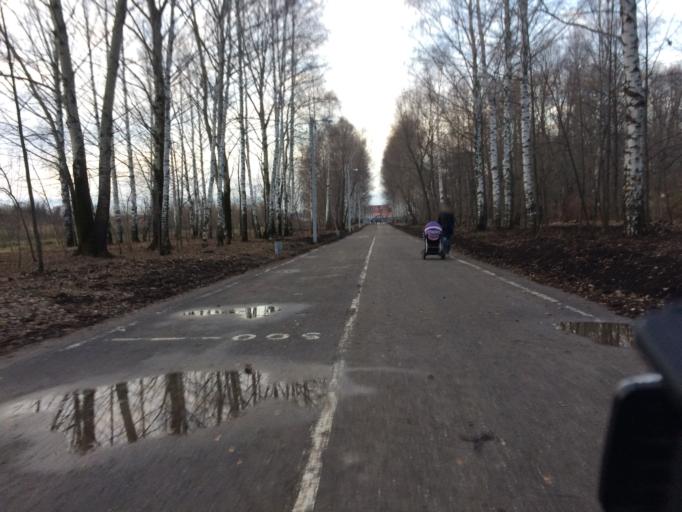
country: RU
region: Mariy-El
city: Yoshkar-Ola
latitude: 56.6240
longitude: 47.9123
